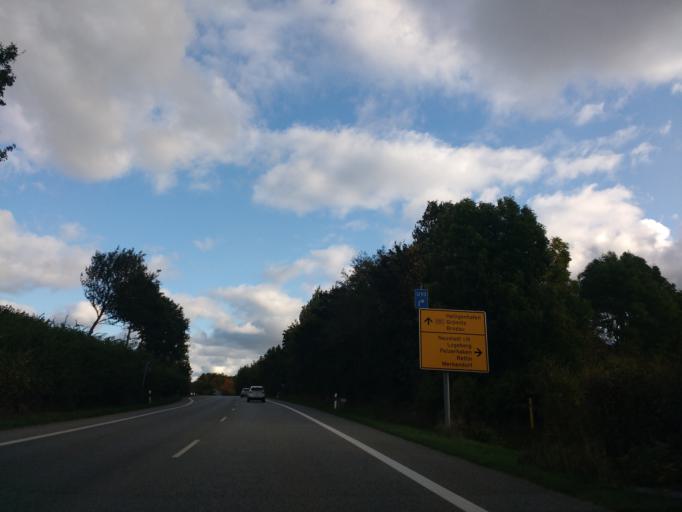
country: DE
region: Schleswig-Holstein
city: Altenkrempe
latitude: 54.1215
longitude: 10.8362
